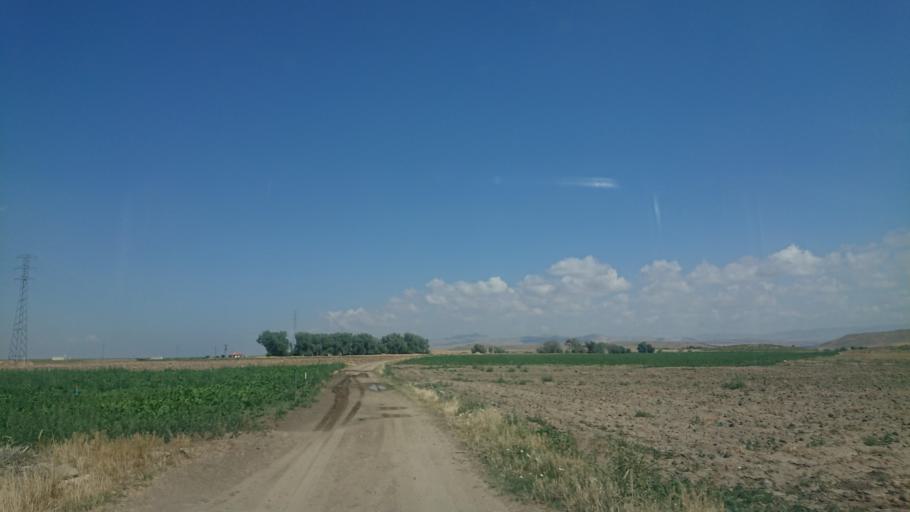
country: TR
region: Aksaray
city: Sariyahsi
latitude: 38.9938
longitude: 33.8962
